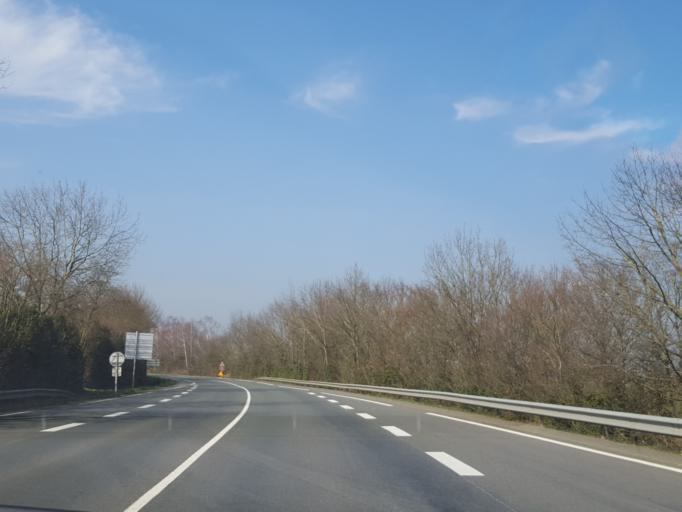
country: FR
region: Pays de la Loire
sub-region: Departement de la Vendee
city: Saint-Fulgent
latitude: 46.8611
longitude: -1.1737
